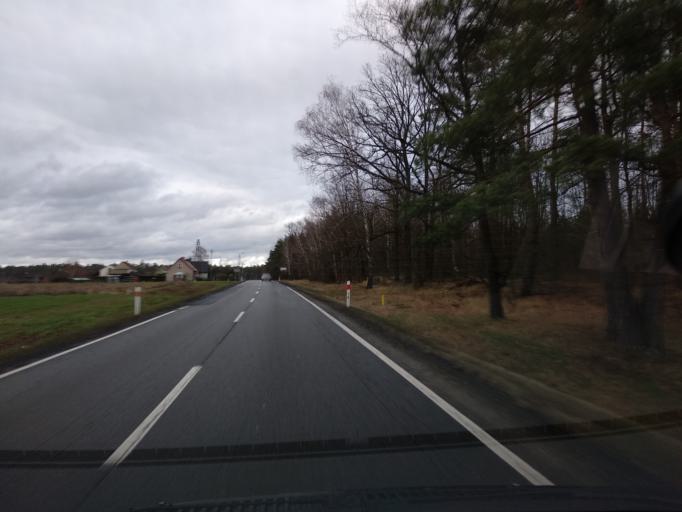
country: PL
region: Lower Silesian Voivodeship
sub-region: Powiat olesnicki
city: Olesnica
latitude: 51.2320
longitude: 17.4487
